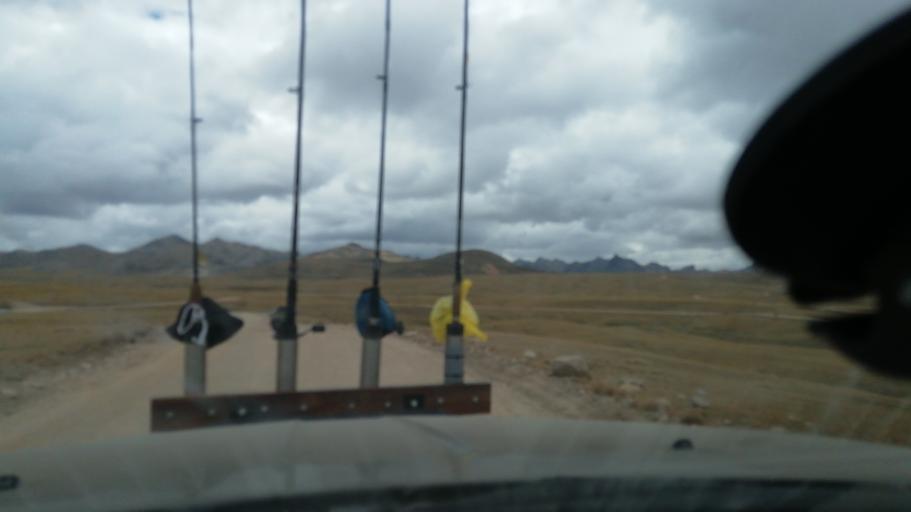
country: PE
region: Huancavelica
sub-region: Provincia de Huancavelica
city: Acobambilla
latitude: -12.5424
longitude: -75.5485
